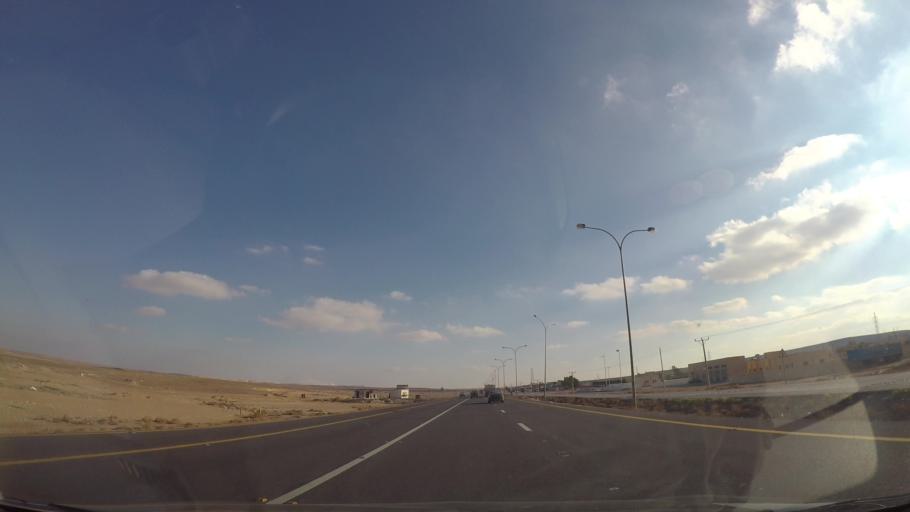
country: JO
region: Karak
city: Karak City
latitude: 31.0808
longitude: 36.0072
